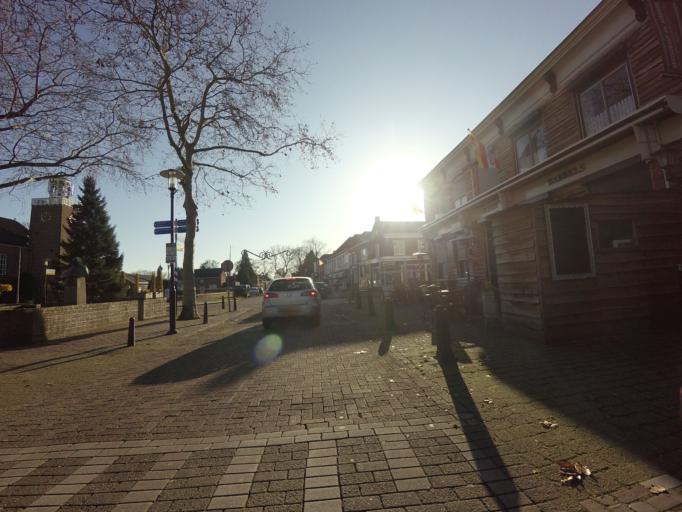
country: NL
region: Gelderland
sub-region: Gemeente Maasdriel
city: Heerewaarden
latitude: 51.7726
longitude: 5.3404
